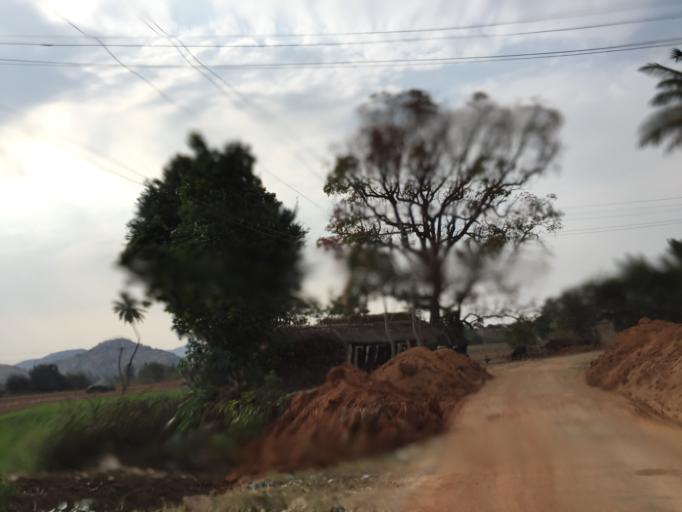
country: IN
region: Karnataka
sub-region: Chikkaballapur
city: Gudibanda
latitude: 13.5748
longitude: 77.7256
